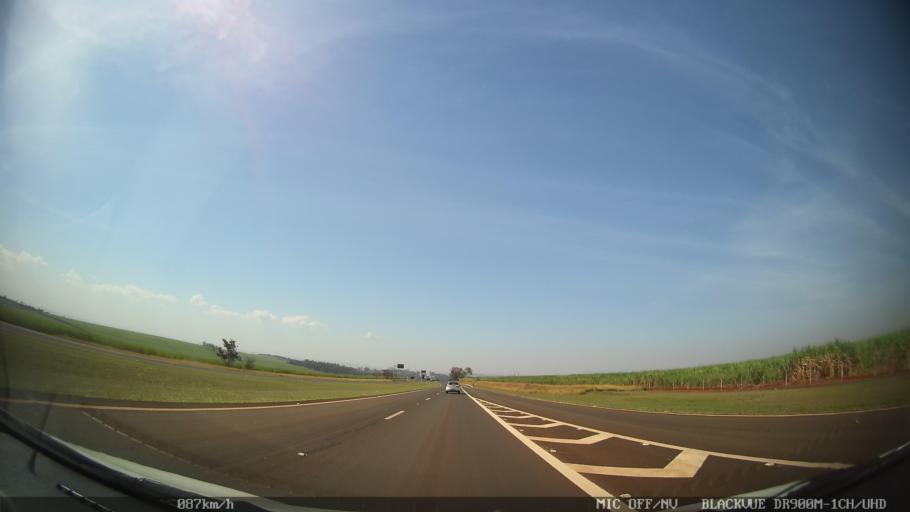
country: BR
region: Sao Paulo
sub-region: Ribeirao Preto
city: Ribeirao Preto
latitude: -21.1666
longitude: -47.8967
